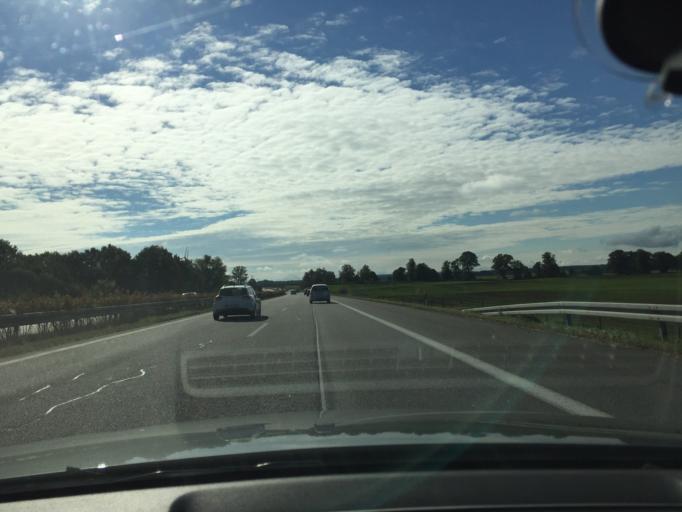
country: DE
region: Mecklenburg-Vorpommern
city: Robel
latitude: 53.3509
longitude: 12.4727
